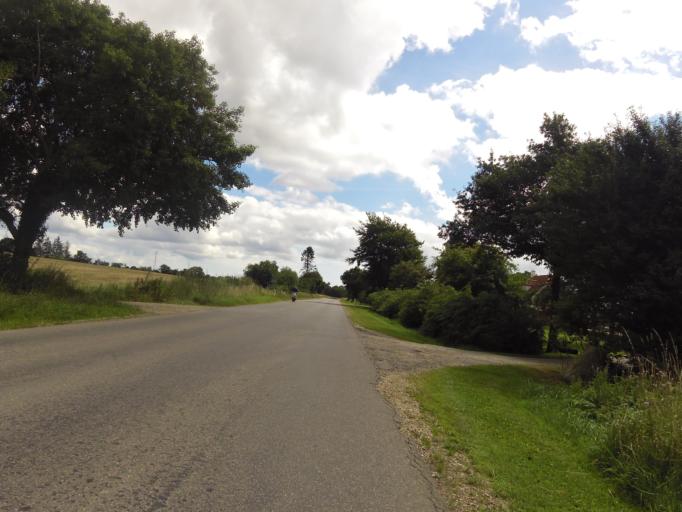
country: DK
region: South Denmark
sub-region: Haderslev Kommune
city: Haderslev
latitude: 55.2782
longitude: 9.4141
